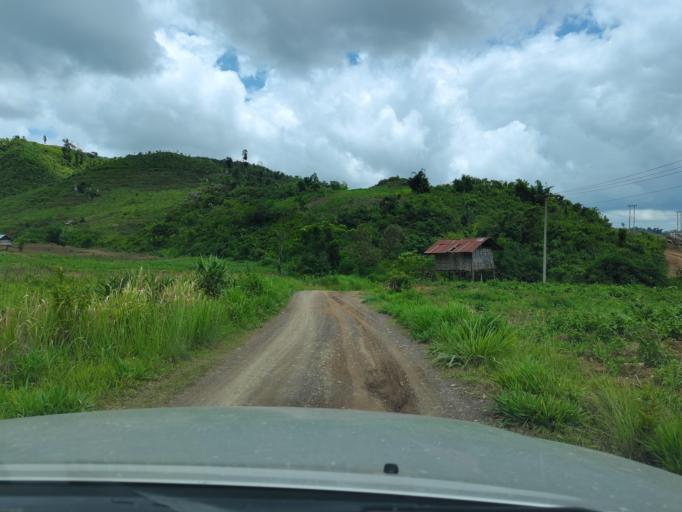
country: LA
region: Loungnamtha
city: Muang Long
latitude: 20.7337
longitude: 101.0142
